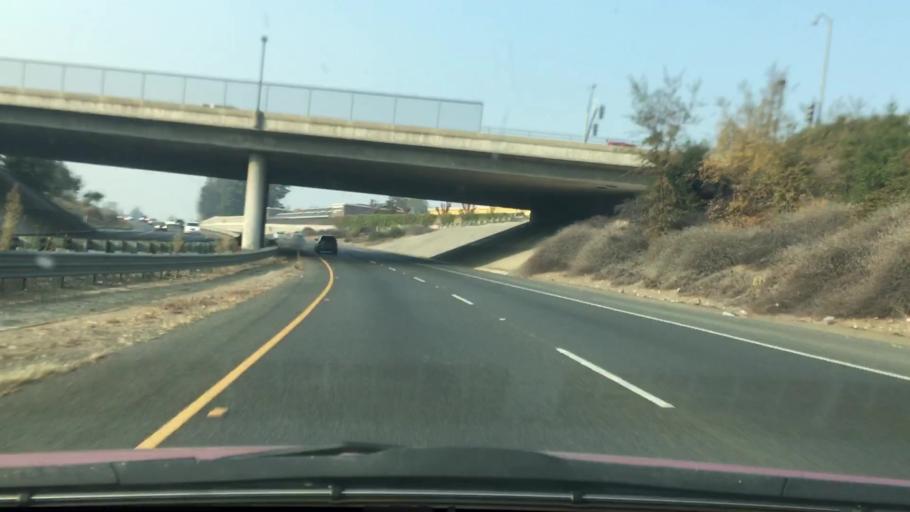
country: US
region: California
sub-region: Napa County
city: Napa
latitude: 38.3210
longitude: -122.3081
